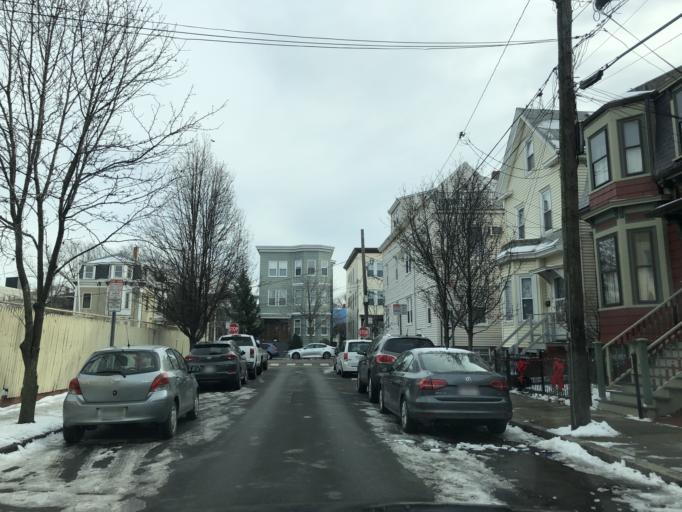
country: US
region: Massachusetts
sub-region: Middlesex County
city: Cambridge
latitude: 42.3746
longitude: -71.0980
